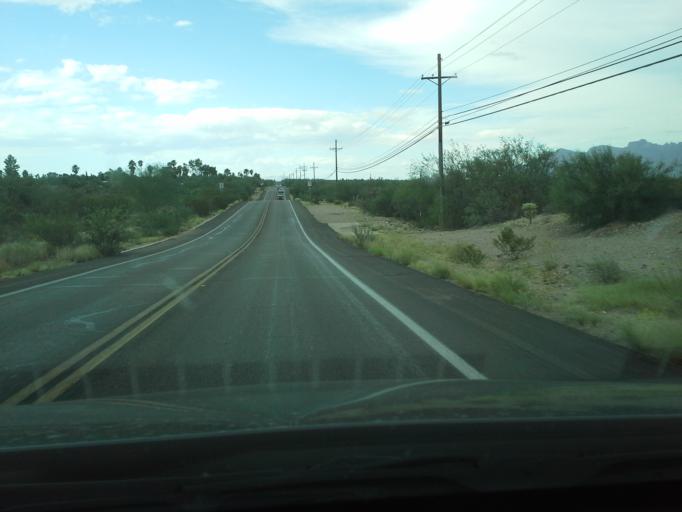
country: US
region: Arizona
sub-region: Pima County
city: South Tucson
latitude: 32.2119
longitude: -111.0203
